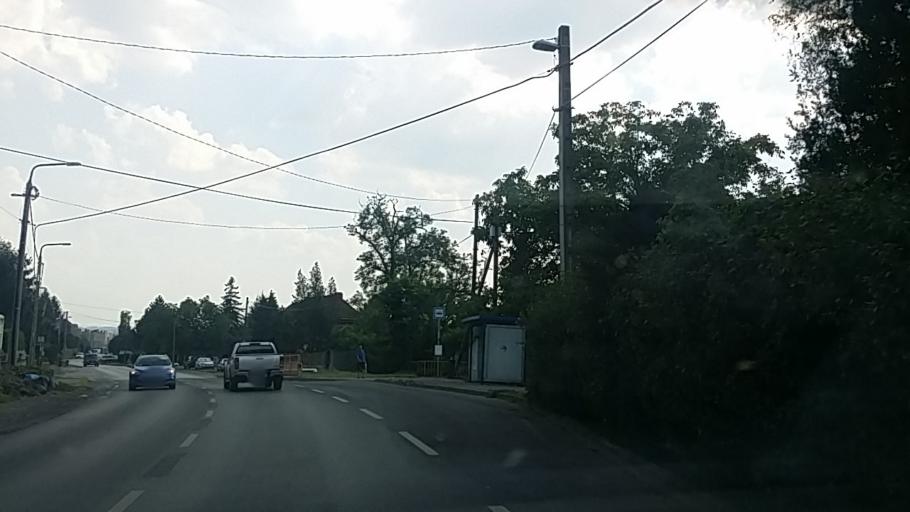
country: HU
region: Baranya
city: Pecs
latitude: 46.0730
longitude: 18.1864
